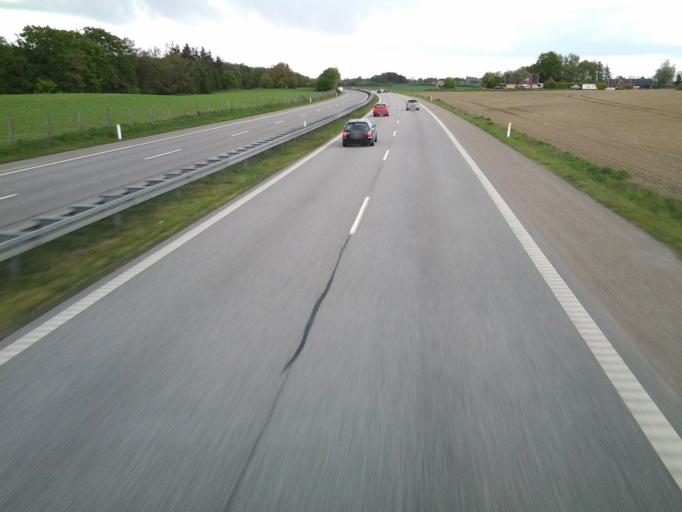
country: DK
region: Zealand
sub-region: Faxe Kommune
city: Ronnede
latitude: 55.1933
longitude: 11.9726
